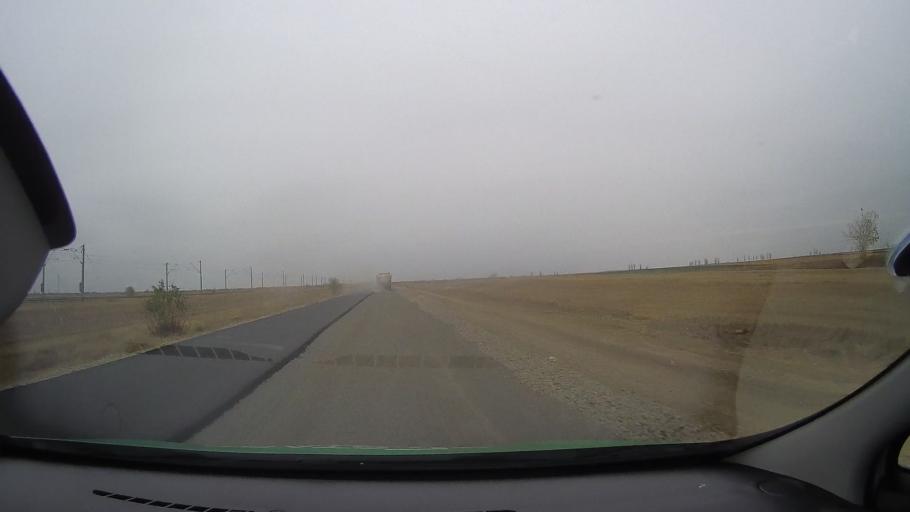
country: RO
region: Braila
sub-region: Comuna Baraganul
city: Baraganul
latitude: 44.7949
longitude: 27.5322
